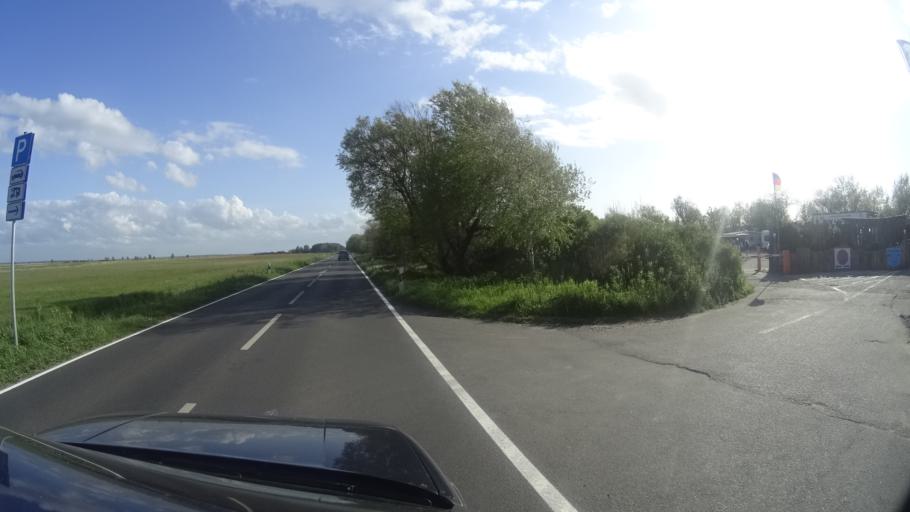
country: DE
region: Mecklenburg-Vorpommern
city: Ostseebad Dierhagen
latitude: 54.3410
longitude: 12.3808
